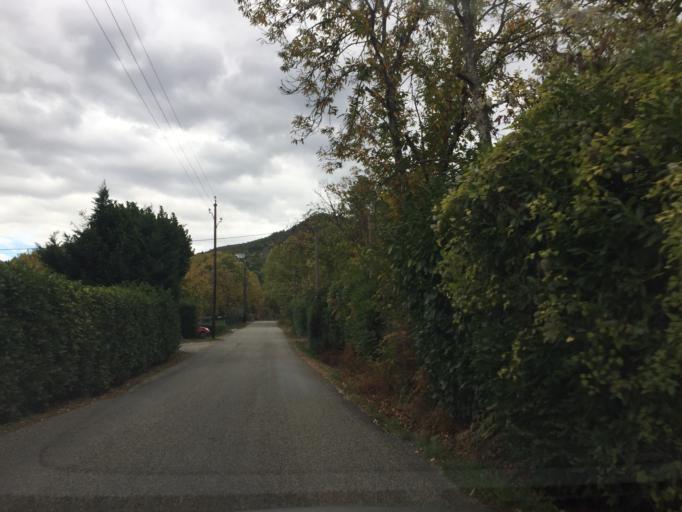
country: FR
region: Rhone-Alpes
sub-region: Departement de l'Ardeche
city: Les Vans
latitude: 44.4151
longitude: 4.0932
